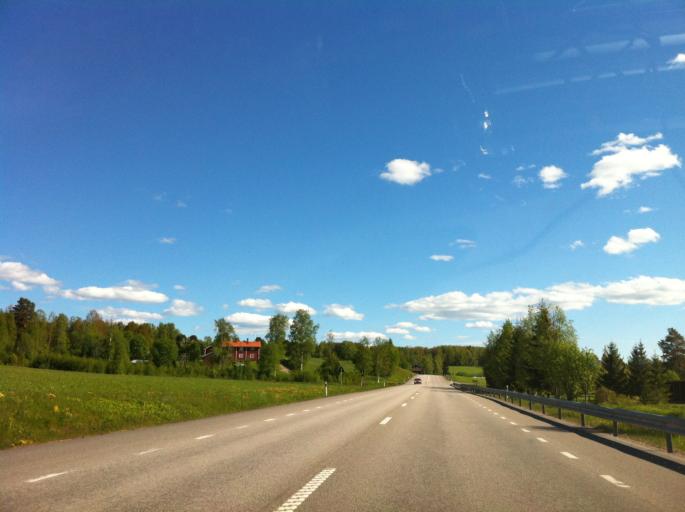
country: SE
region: Dalarna
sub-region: Rattviks Kommun
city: Raettvik
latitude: 60.8568
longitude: 15.1022
